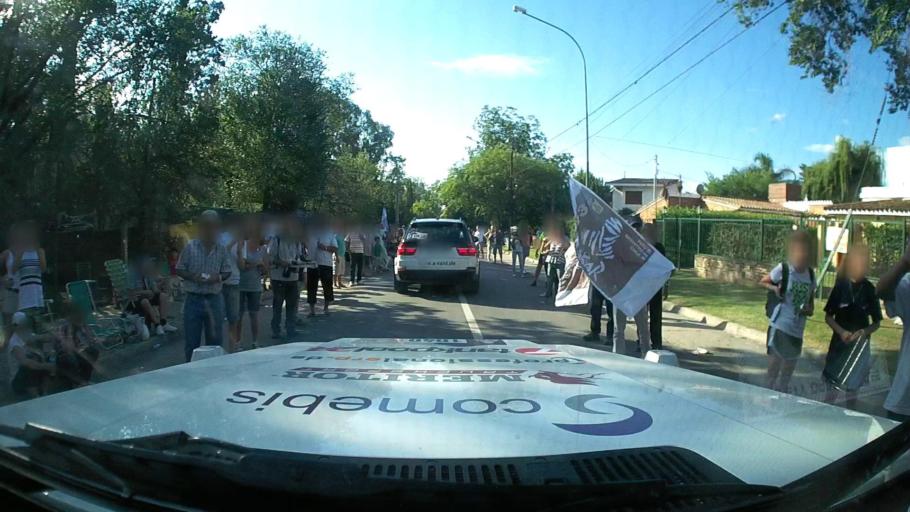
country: AR
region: Cordoba
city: Villa Carlos Paz
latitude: -31.3994
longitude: -64.4678
